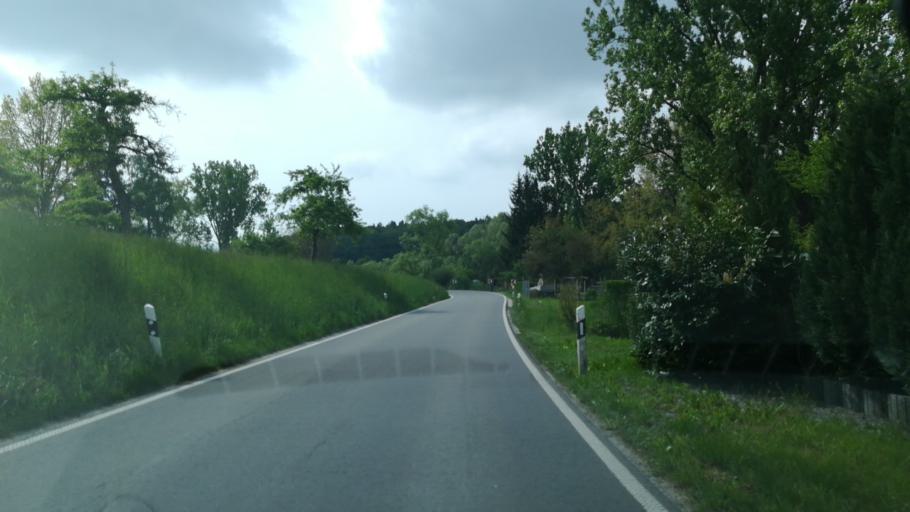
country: DE
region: Baden-Wuerttemberg
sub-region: Freiburg Region
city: Volkertshausen
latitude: 47.7827
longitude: 8.8793
